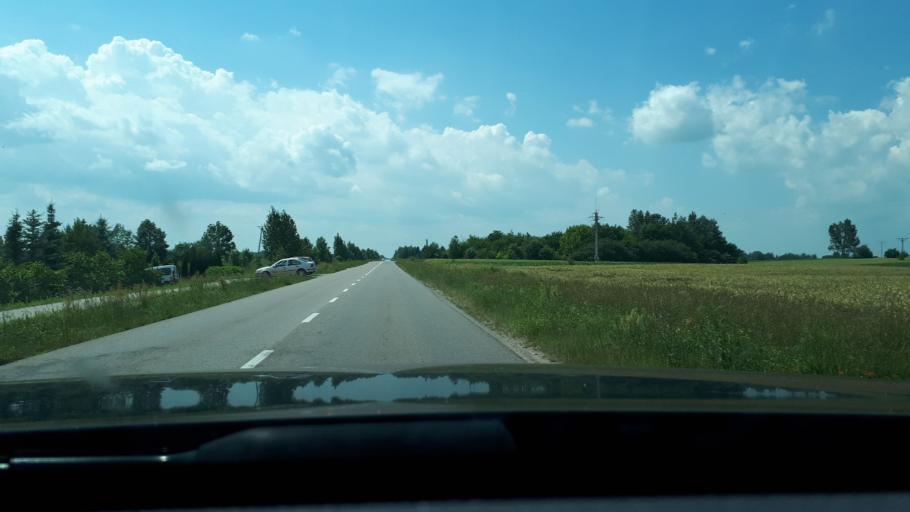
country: PL
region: Podlasie
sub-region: Powiat bialostocki
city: Choroszcz
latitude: 53.1296
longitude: 23.0211
